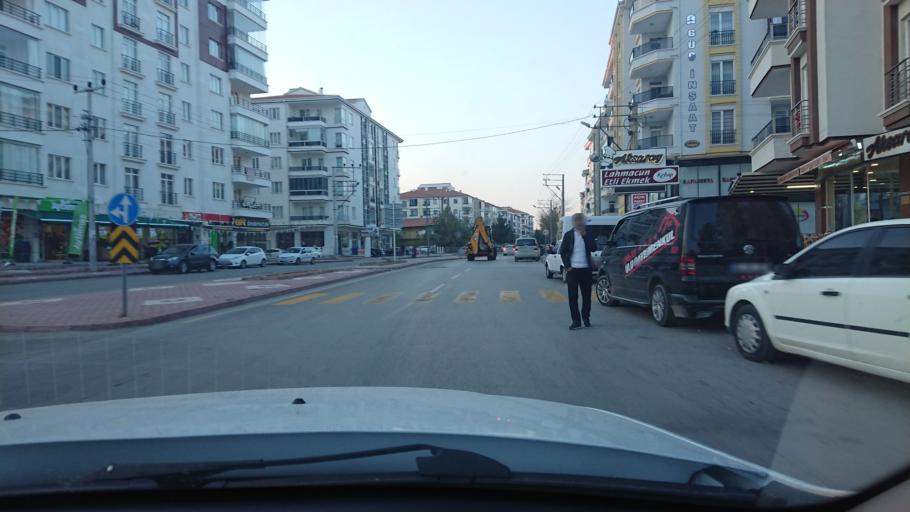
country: TR
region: Aksaray
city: Aksaray
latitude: 38.3595
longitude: 34.0388
